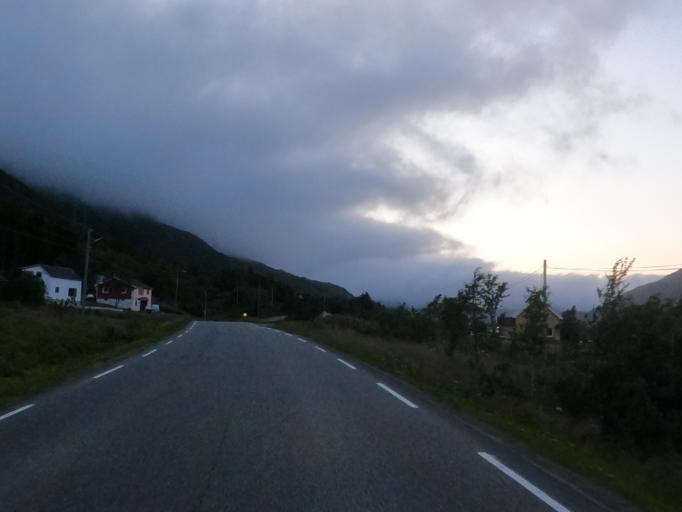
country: NO
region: Nordland
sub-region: Lodingen
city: Lodingen
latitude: 68.5757
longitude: 15.7946
